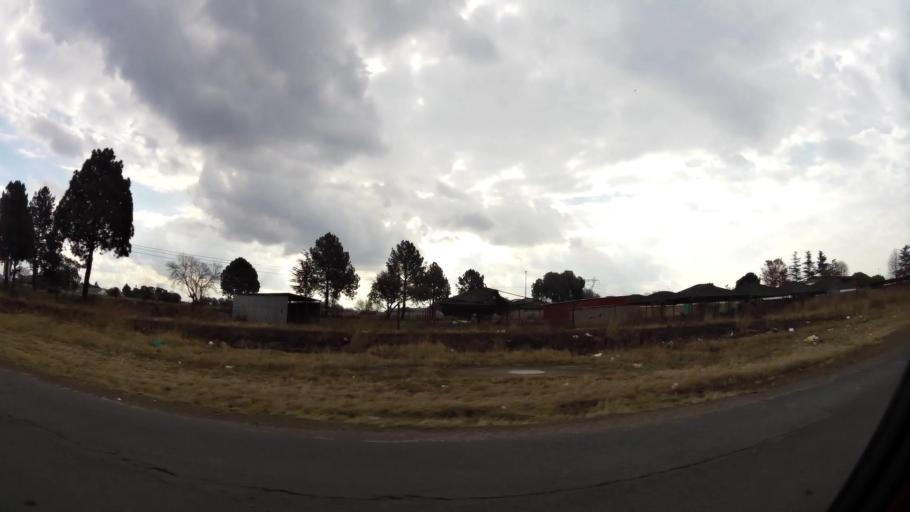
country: ZA
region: Gauteng
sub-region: Sedibeng District Municipality
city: Vanderbijlpark
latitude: -26.6607
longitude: 27.8449
